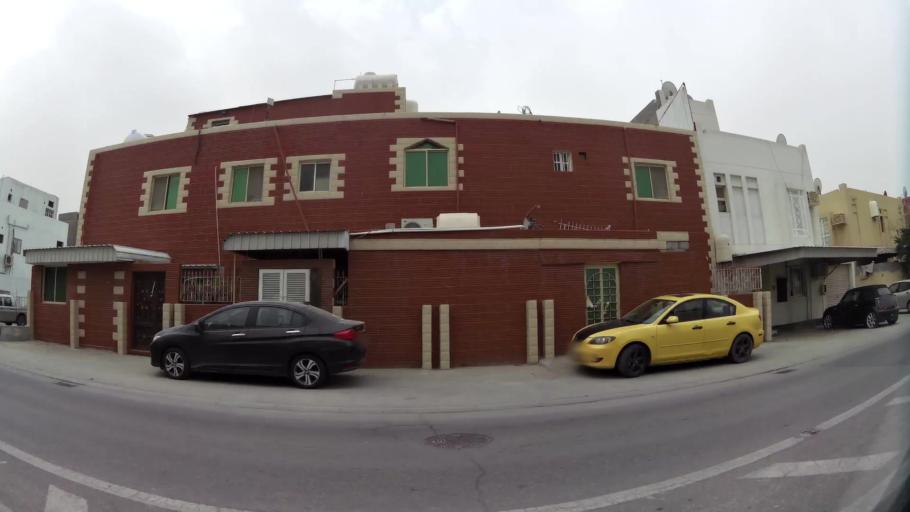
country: BH
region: Northern
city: Madinat `Isa
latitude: 26.1787
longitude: 50.5425
